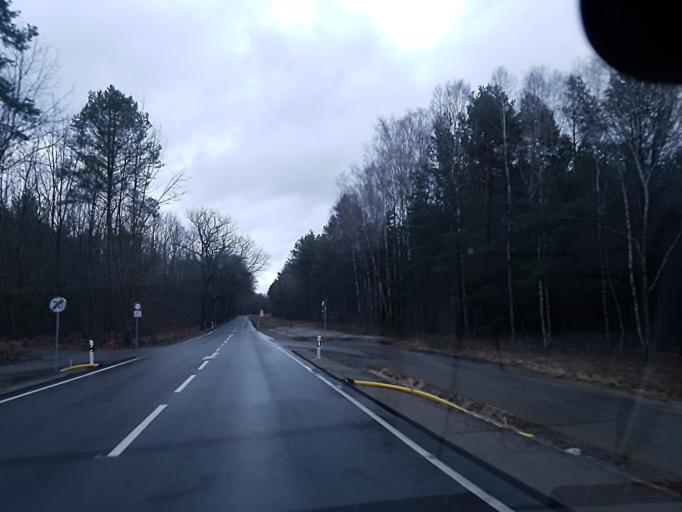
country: DE
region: Brandenburg
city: Hohenleipisch
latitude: 51.5239
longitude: 13.5785
